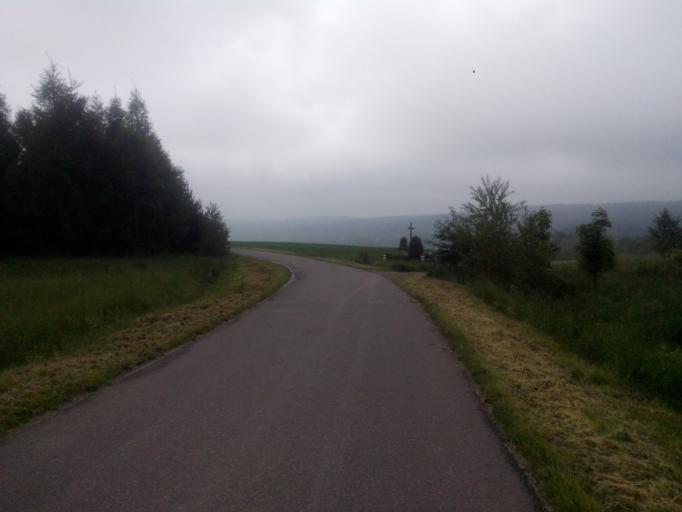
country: PL
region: Subcarpathian Voivodeship
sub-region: Powiat strzyzowski
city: Wysoka Strzyzowska
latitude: 49.8048
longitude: 21.7818
